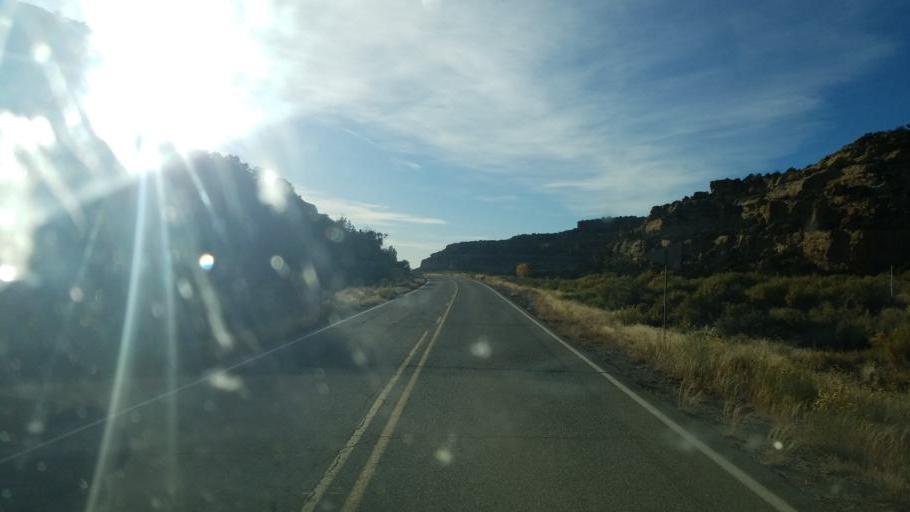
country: US
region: New Mexico
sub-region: San Juan County
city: Bloomfield
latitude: 36.7402
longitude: -107.7222
